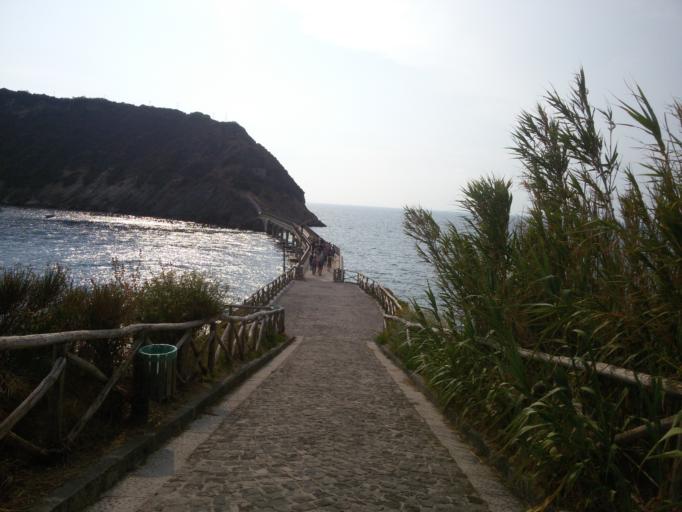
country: IT
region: Campania
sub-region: Provincia di Napoli
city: Procida
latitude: 40.7476
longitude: 14.0005
